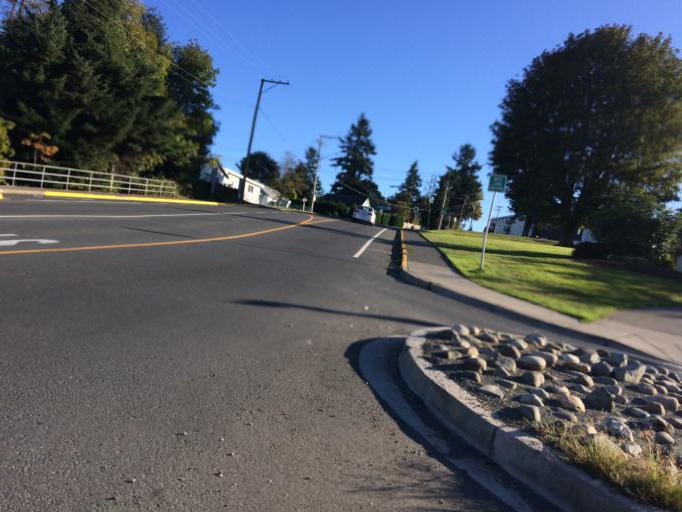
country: CA
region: British Columbia
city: Campbell River
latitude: 50.0241
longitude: -125.2431
